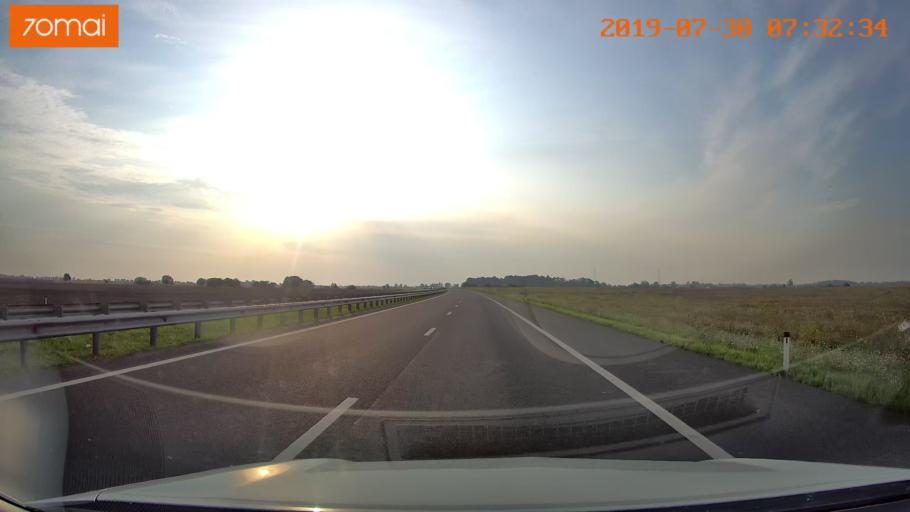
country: RU
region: Kaliningrad
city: Gvardeysk
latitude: 54.6672
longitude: 21.0231
